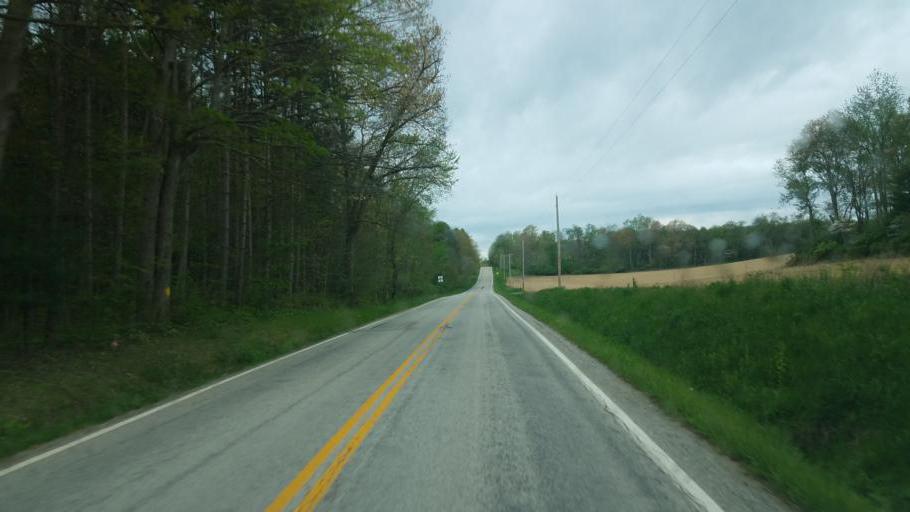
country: US
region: Ohio
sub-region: Ashland County
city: Loudonville
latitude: 40.6238
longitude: -82.3037
